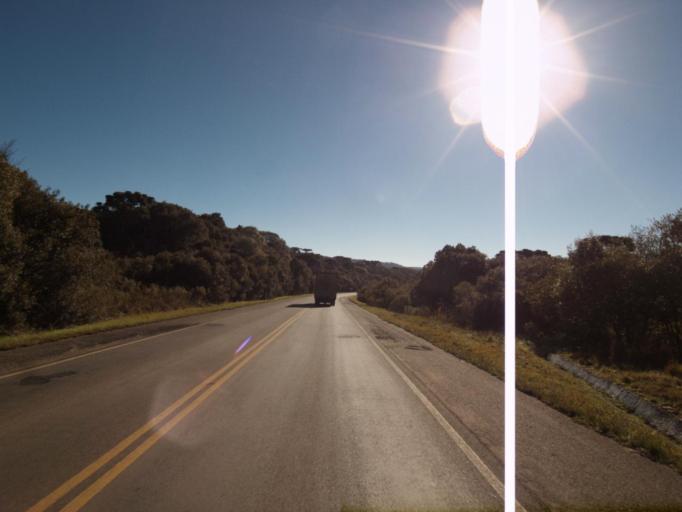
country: BR
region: Santa Catarina
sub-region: Concordia
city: Concordia
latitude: -26.9418
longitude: -51.8227
